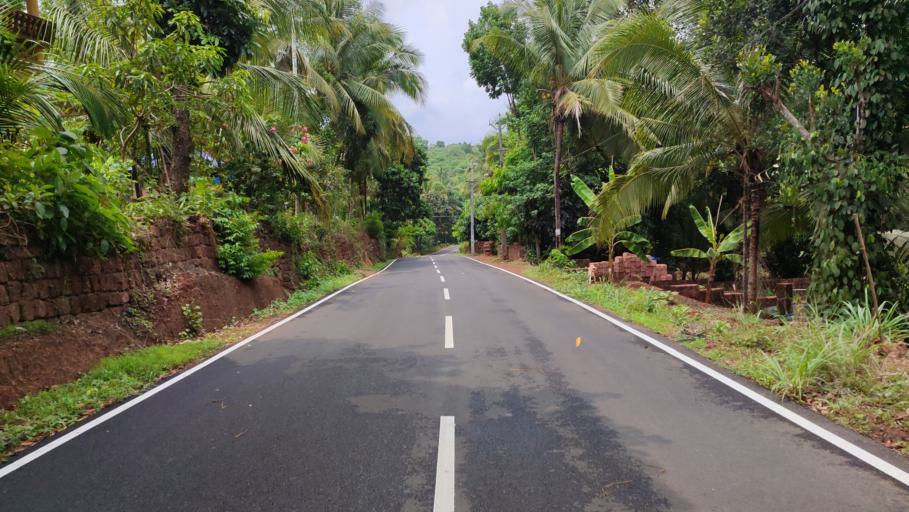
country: IN
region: Kerala
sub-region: Kasaragod District
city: Kannangad
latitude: 12.3186
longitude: 75.1493
